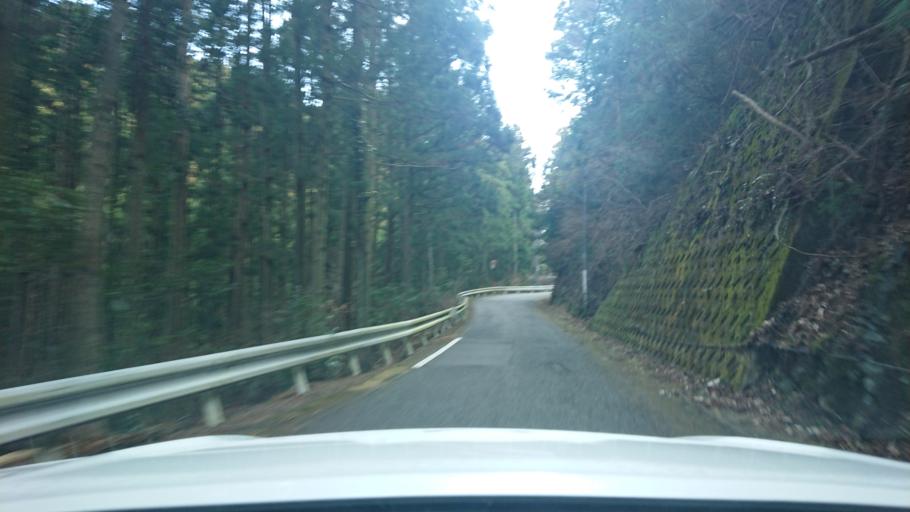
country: JP
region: Tokushima
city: Ishii
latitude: 33.9134
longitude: 134.3993
